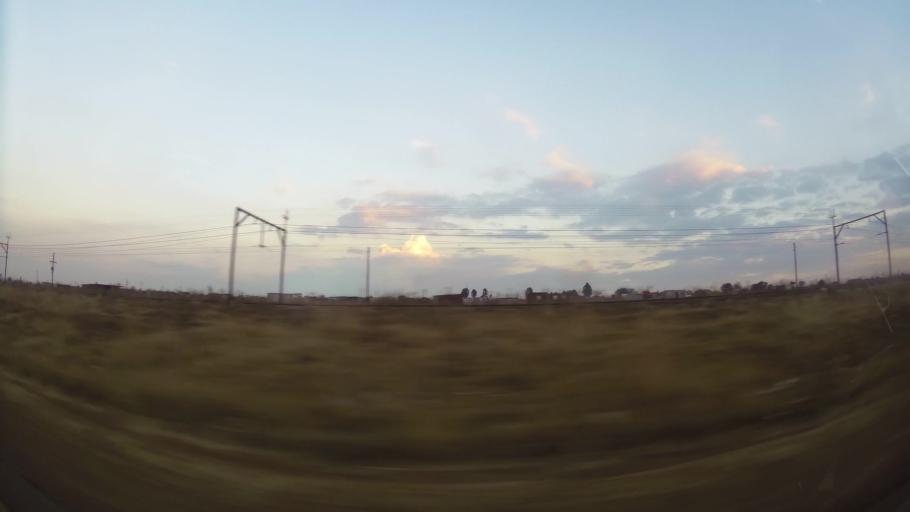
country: ZA
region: Gauteng
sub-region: City of Johannesburg Metropolitan Municipality
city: Orange Farm
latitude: -26.5630
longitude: 27.8693
